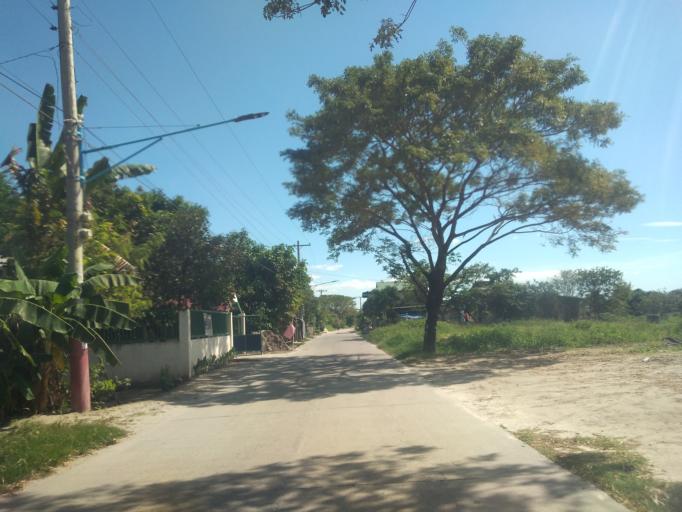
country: PH
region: Central Luzon
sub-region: Province of Pampanga
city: Bacolor
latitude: 15.0146
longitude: 120.6423
